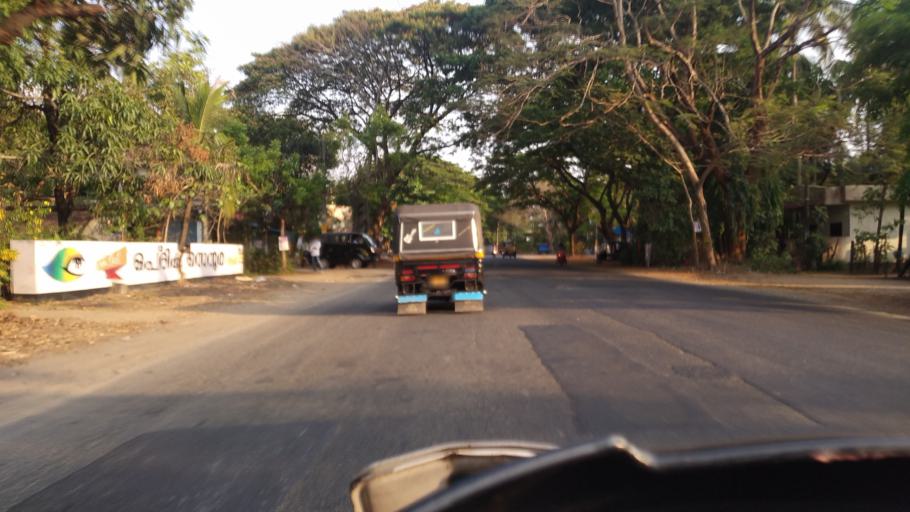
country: IN
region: Kerala
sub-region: Thrissur District
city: Thanniyam
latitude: 10.4322
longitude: 76.0992
